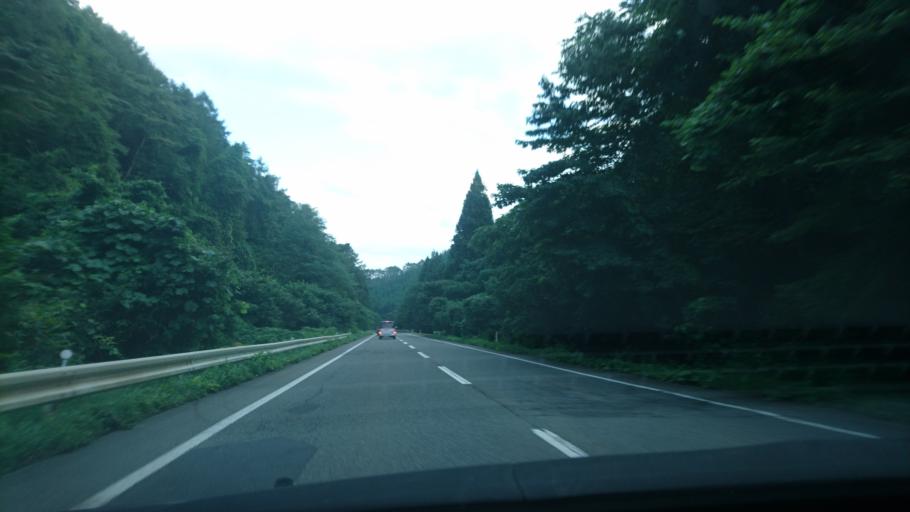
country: JP
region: Iwate
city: Mizusawa
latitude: 39.0538
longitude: 141.2270
